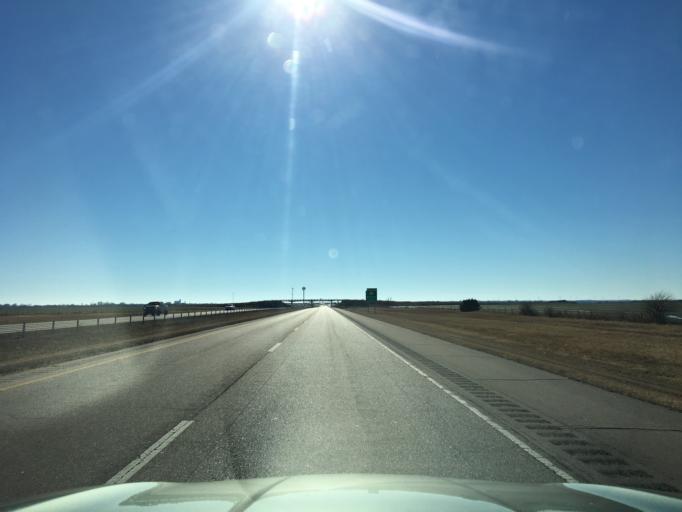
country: US
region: Oklahoma
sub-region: Kay County
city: Blackwell
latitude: 36.9606
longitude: -97.3458
